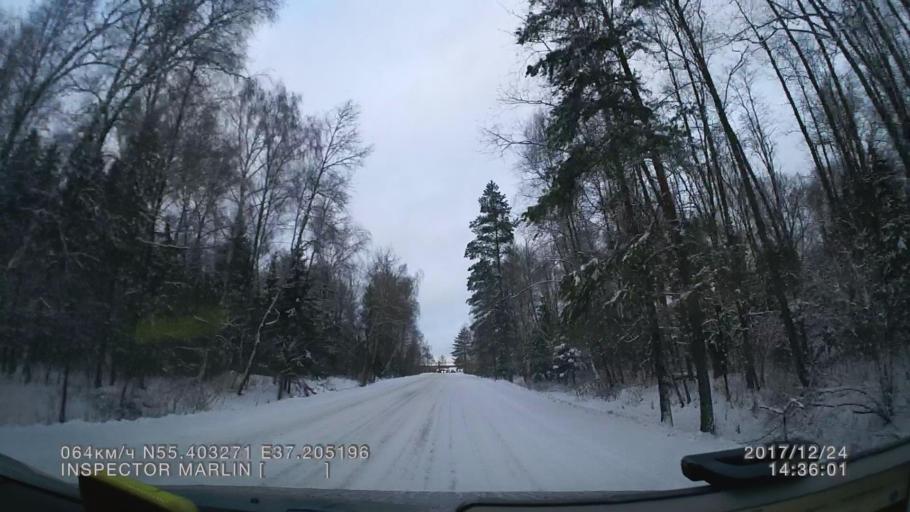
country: RU
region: Moskovskaya
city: Troitsk
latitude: 55.4032
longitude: 37.2052
